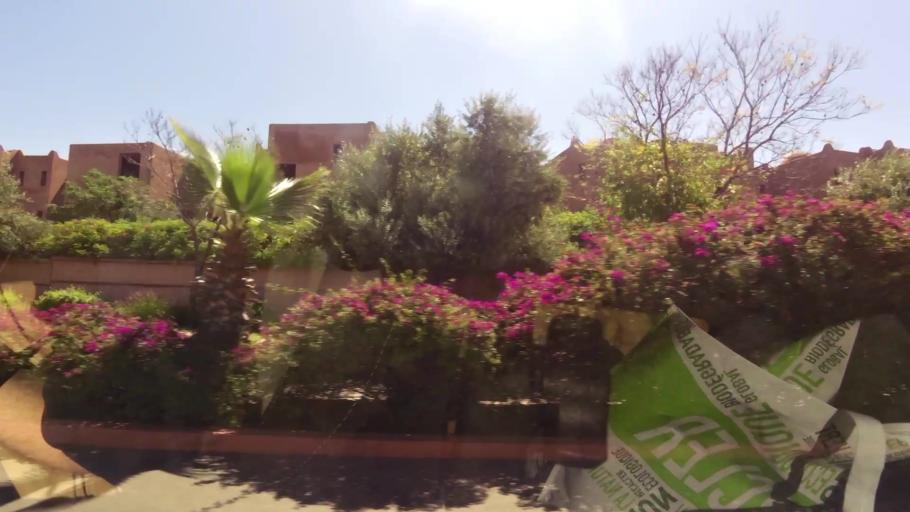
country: MA
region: Marrakech-Tensift-Al Haouz
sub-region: Marrakech
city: Marrakesh
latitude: 31.6001
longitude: -7.9907
